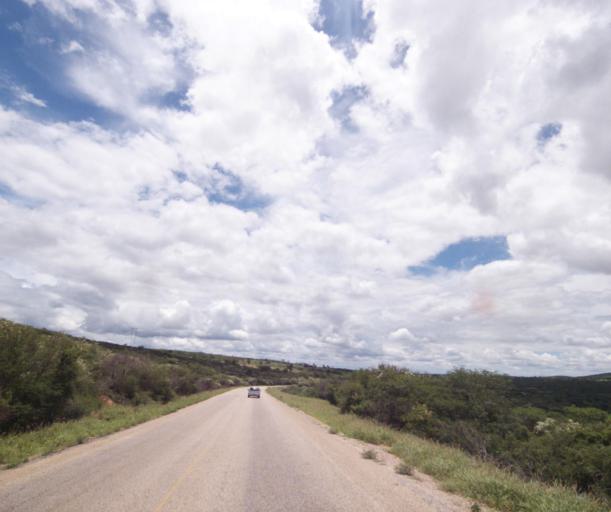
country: BR
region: Bahia
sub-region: Brumado
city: Brumado
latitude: -14.2019
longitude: -41.6182
